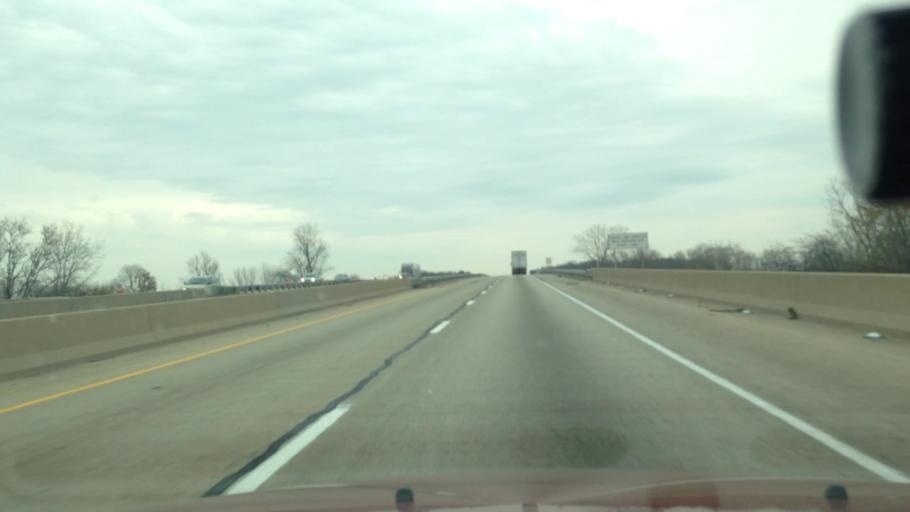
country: US
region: Indiana
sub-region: Wayne County
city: Cambridge City
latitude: 39.8522
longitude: -85.2484
